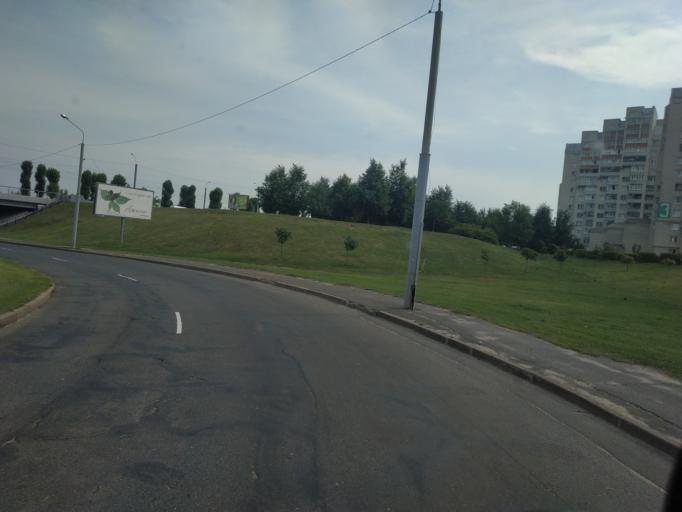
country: BY
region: Mogilev
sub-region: Mahilyowski Rayon
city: Veyno
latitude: 53.8772
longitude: 30.3846
